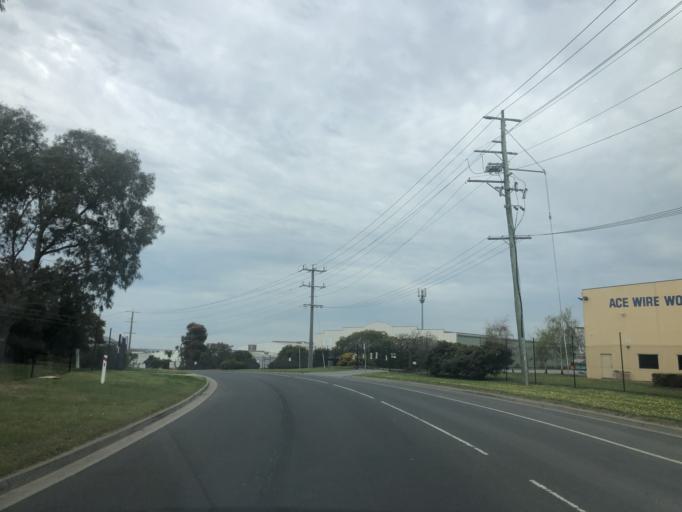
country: AU
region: Victoria
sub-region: Casey
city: Hallam
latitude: -38.0093
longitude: 145.2630
